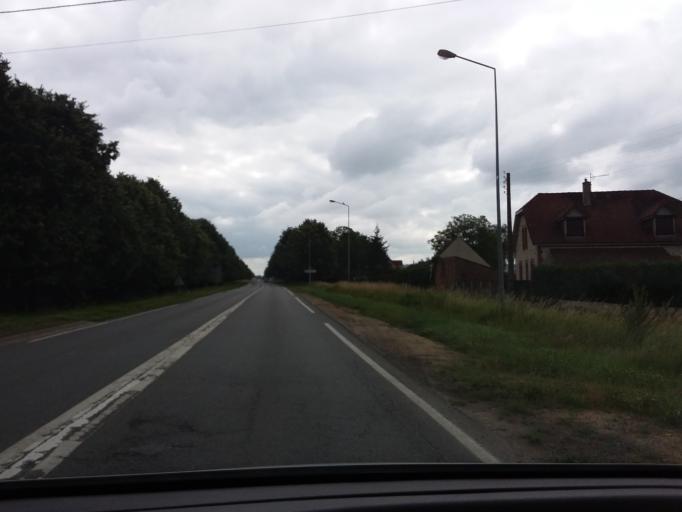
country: FR
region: Picardie
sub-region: Departement de l'Aisne
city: Bucy-le-Long
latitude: 49.3874
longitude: 3.3939
